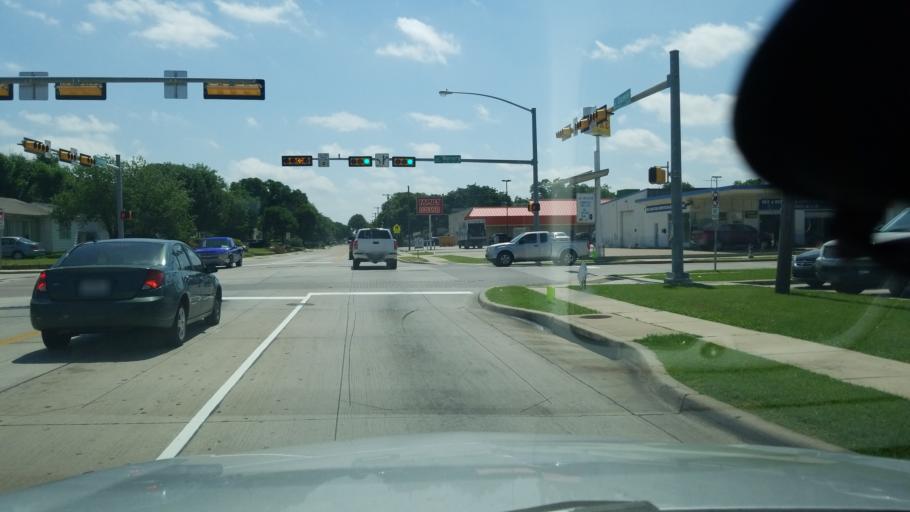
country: US
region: Texas
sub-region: Dallas County
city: Irving
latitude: 32.8296
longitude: -96.9357
